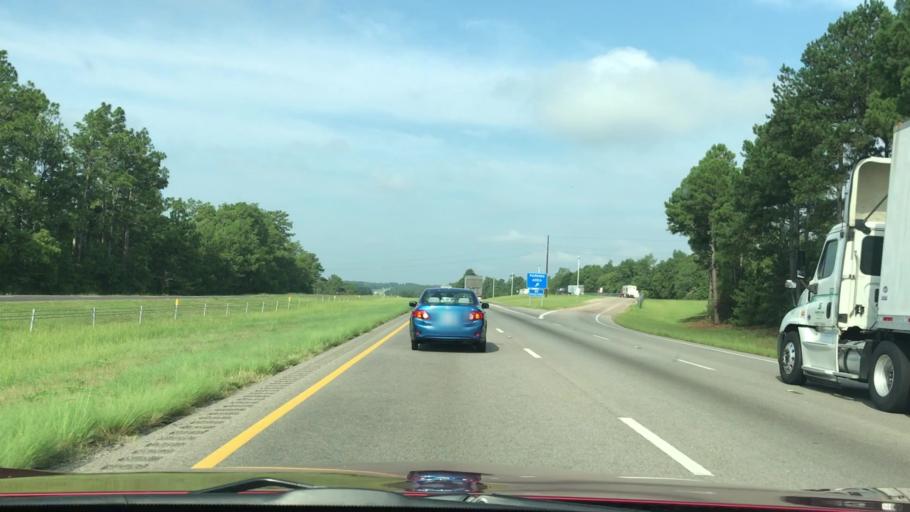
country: US
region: South Carolina
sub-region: Aiken County
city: Aiken
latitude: 33.6548
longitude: -81.7031
